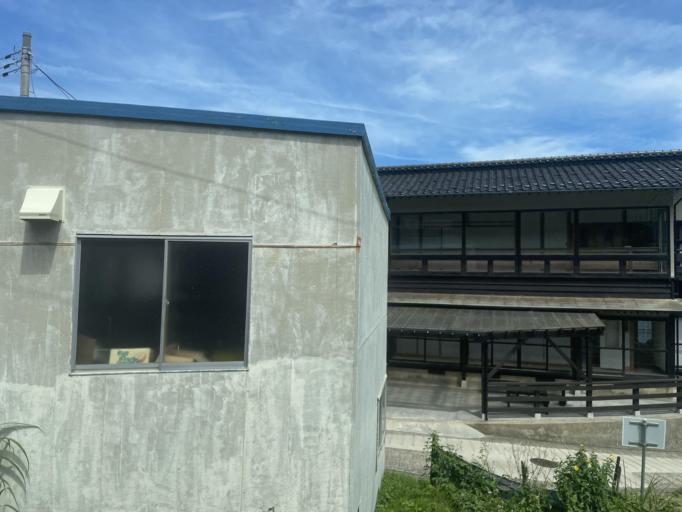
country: JP
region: Yamagata
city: Tsuruoka
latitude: 38.6883
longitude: 139.6433
